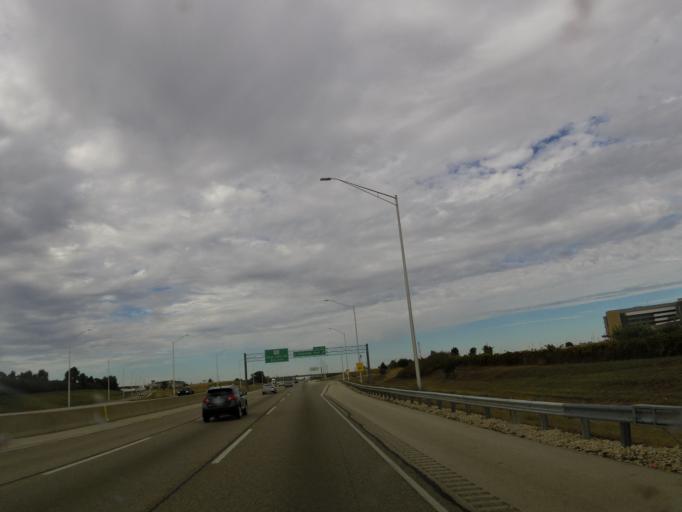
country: US
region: Illinois
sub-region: Winnebago County
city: Cherry Valley
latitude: 42.3126
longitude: -88.9646
